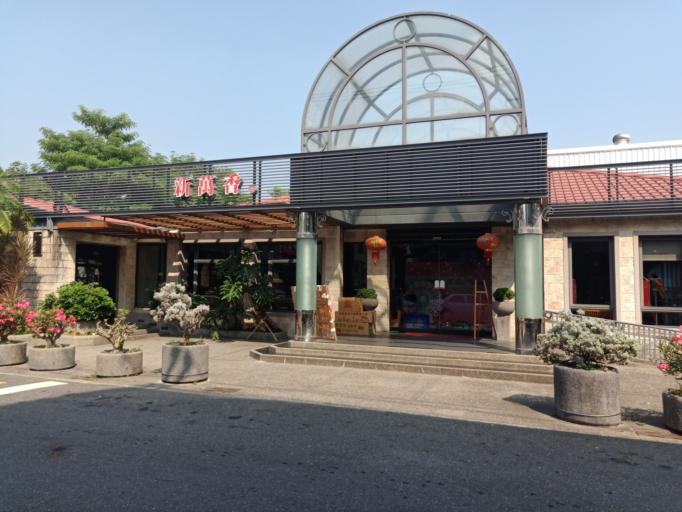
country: TW
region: Taiwan
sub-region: Tainan
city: Tainan
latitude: 23.1301
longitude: 120.2950
